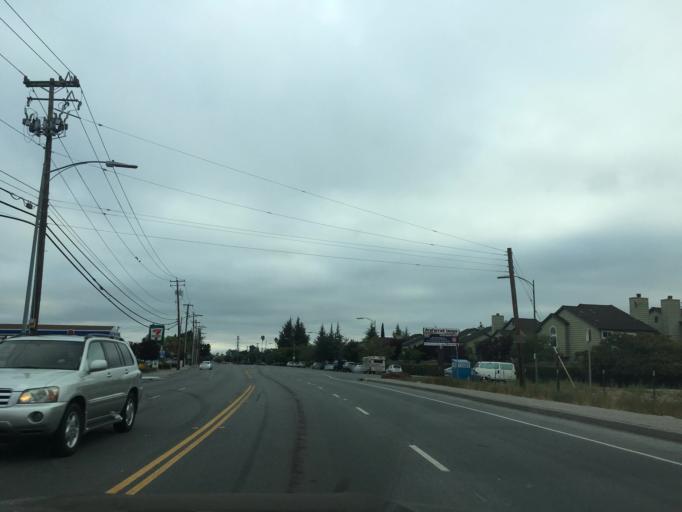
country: US
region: California
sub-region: Santa Clara County
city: Cambrian Park
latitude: 37.2316
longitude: -121.9036
